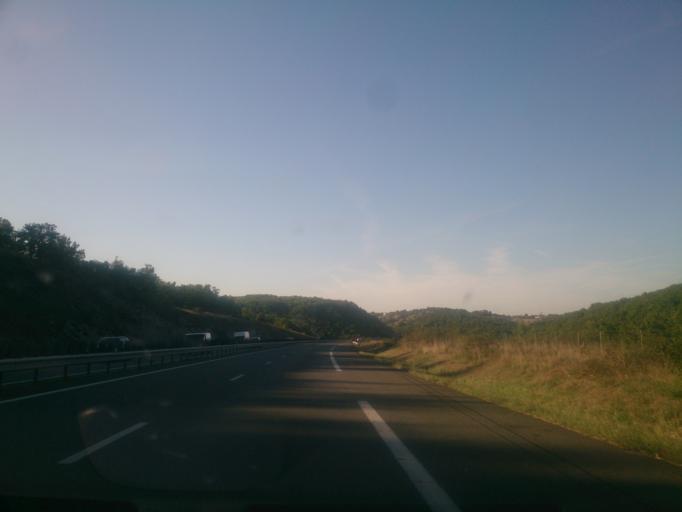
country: FR
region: Midi-Pyrenees
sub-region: Departement du Lot
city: Le Vigan
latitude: 44.7280
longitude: 1.5575
